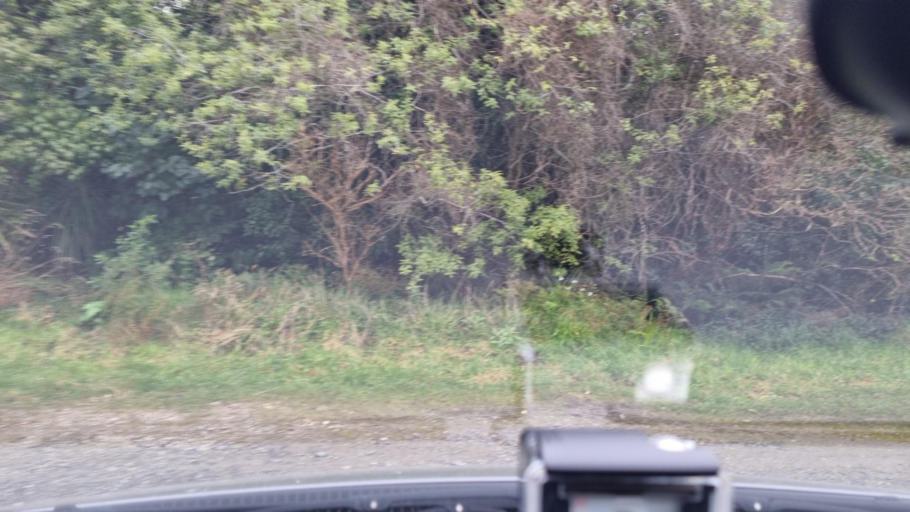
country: NZ
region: Southland
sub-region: Invercargill City
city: Bluff
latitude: -46.6111
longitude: 168.3524
